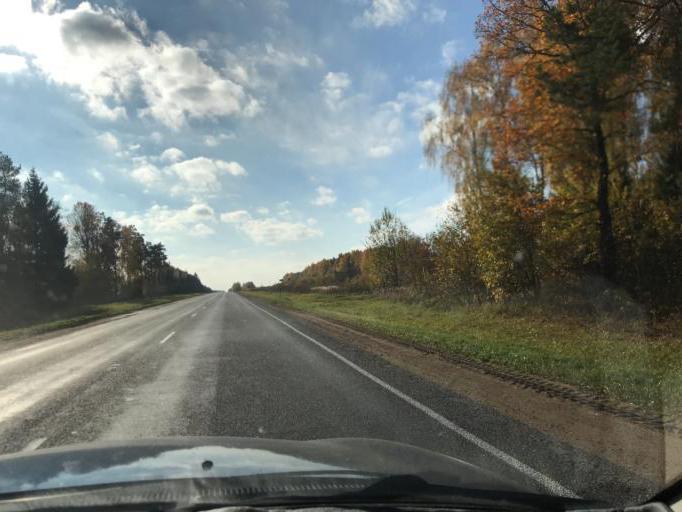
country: BY
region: Grodnenskaya
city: Voranava
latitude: 54.2164
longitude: 25.3535
